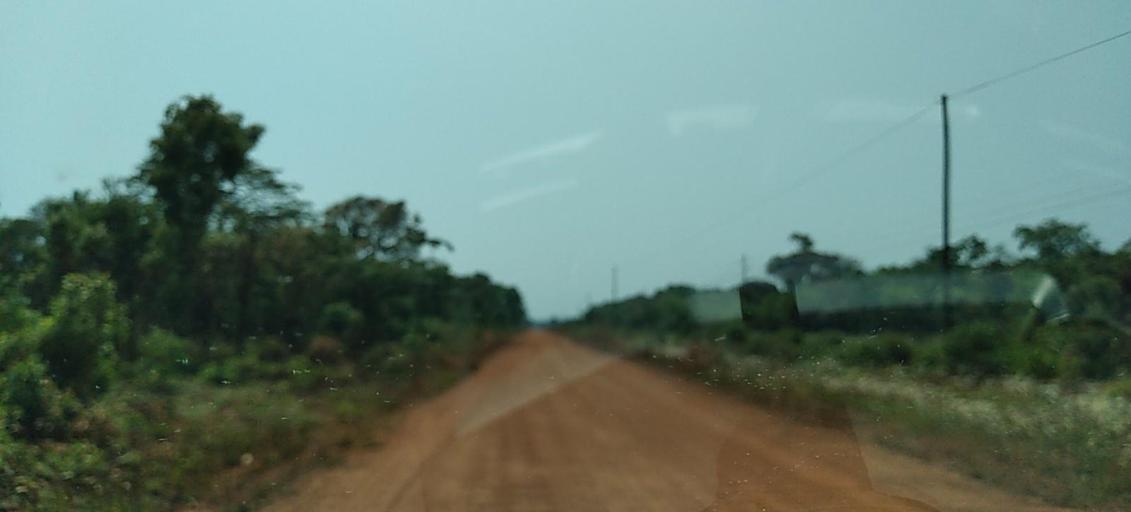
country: ZM
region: North-Western
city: Kansanshi
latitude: -11.9943
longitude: 26.6462
